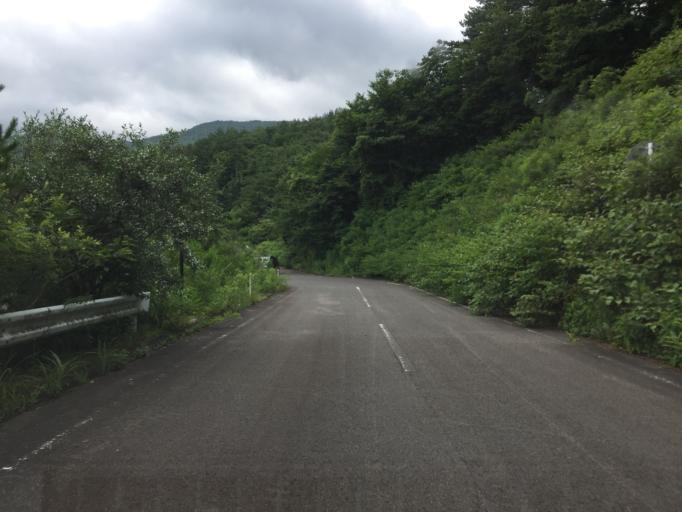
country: JP
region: Fukushima
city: Nihommatsu
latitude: 37.6600
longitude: 140.3291
